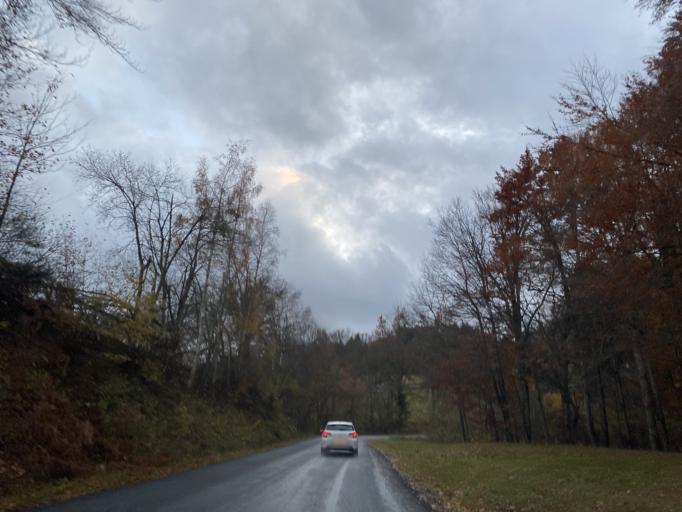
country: FR
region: Auvergne
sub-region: Departement du Puy-de-Dome
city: Cunlhat
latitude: 45.6070
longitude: 3.5706
